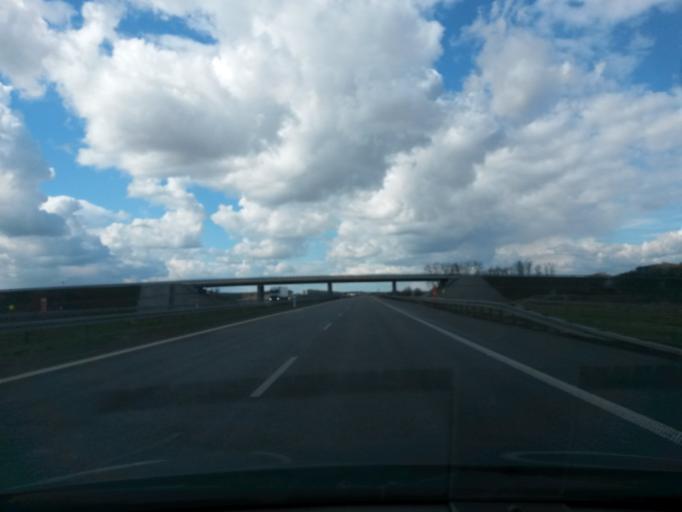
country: PL
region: Greater Poland Voivodeship
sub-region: Powiat kolski
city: Dabie
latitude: 52.1052
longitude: 18.7535
